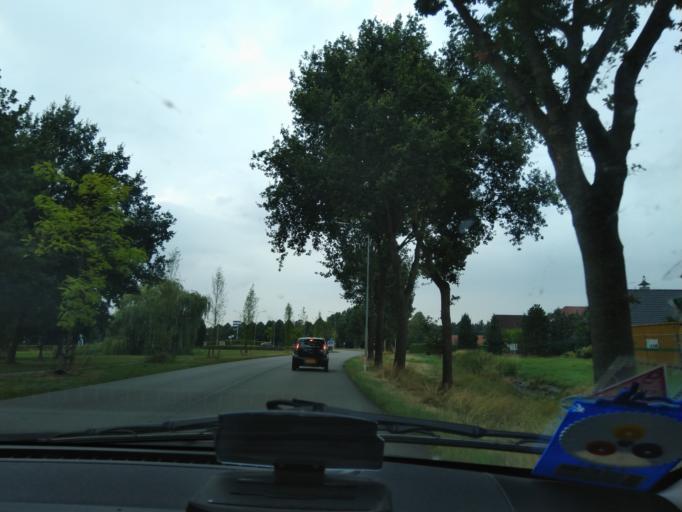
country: NL
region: Groningen
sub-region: Gemeente Pekela
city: Oude Pekela
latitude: 53.1135
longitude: 7.0235
